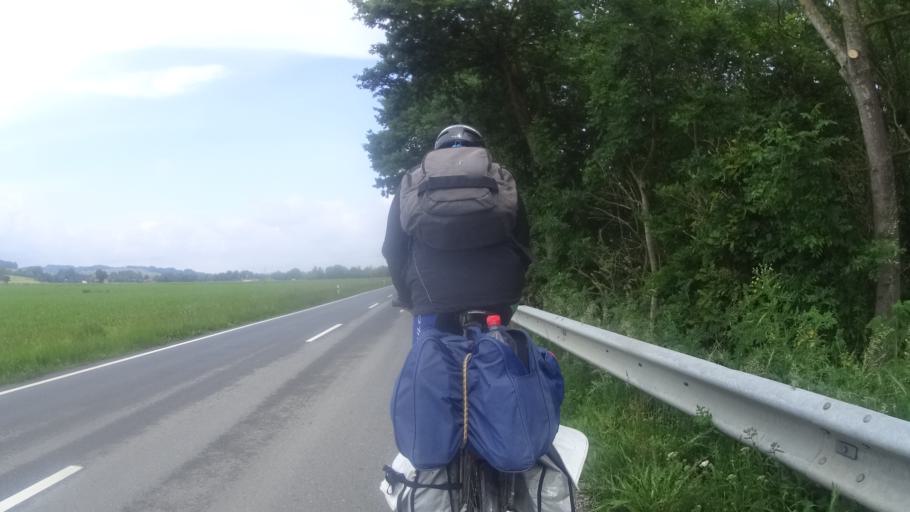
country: DE
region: Bavaria
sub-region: Lower Bavaria
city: Bayerbach
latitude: 48.4274
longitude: 13.1176
